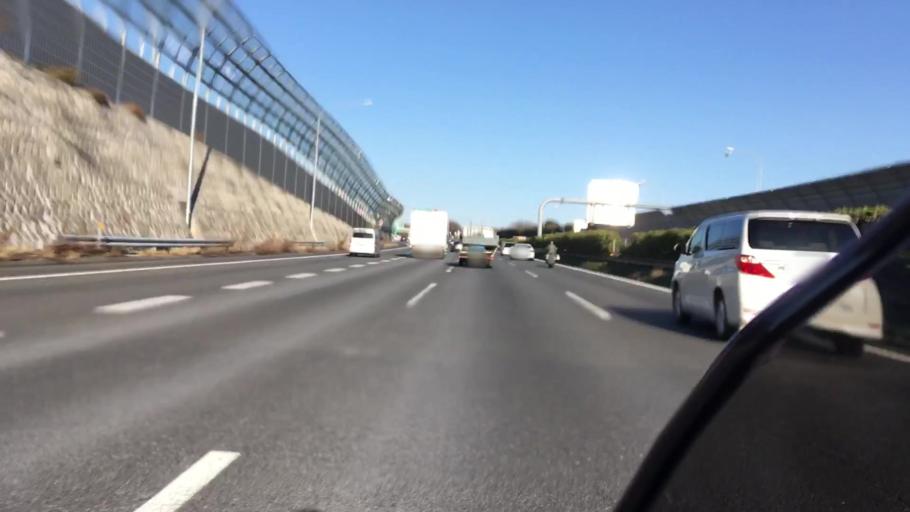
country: JP
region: Kanagawa
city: Atsugi
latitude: 35.4276
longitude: 139.3946
